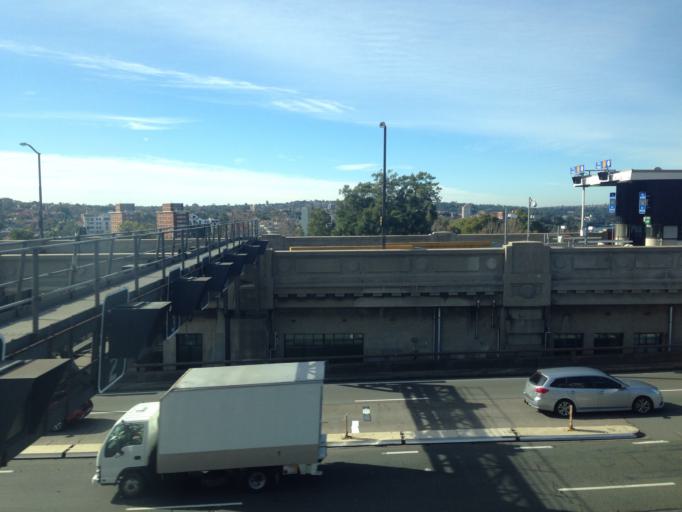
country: AU
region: New South Wales
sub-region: North Sydney
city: Milsons Point
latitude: -33.8452
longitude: 151.2116
